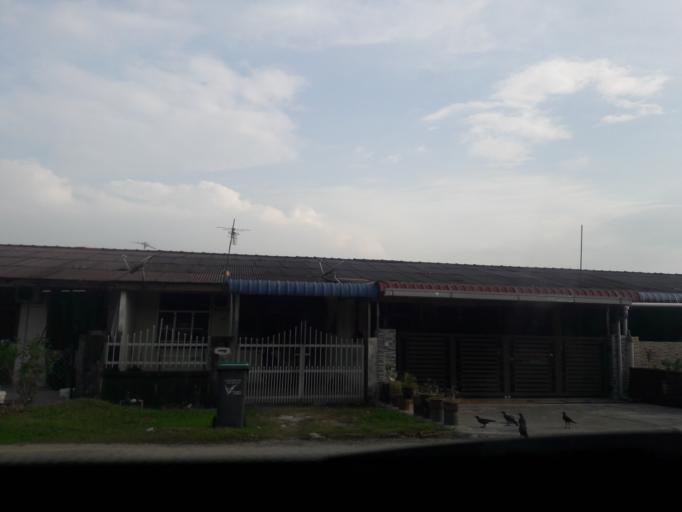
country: MY
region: Kedah
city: Kulim
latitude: 5.3784
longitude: 100.5327
